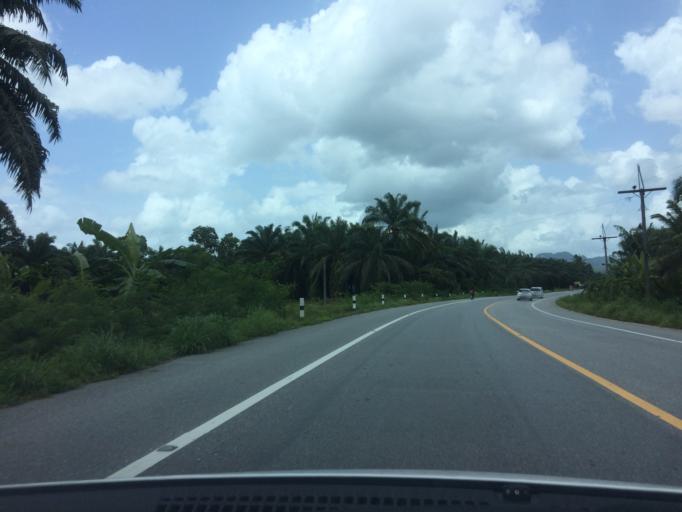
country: TH
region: Phangnga
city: Thap Put
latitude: 8.4774
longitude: 98.6600
